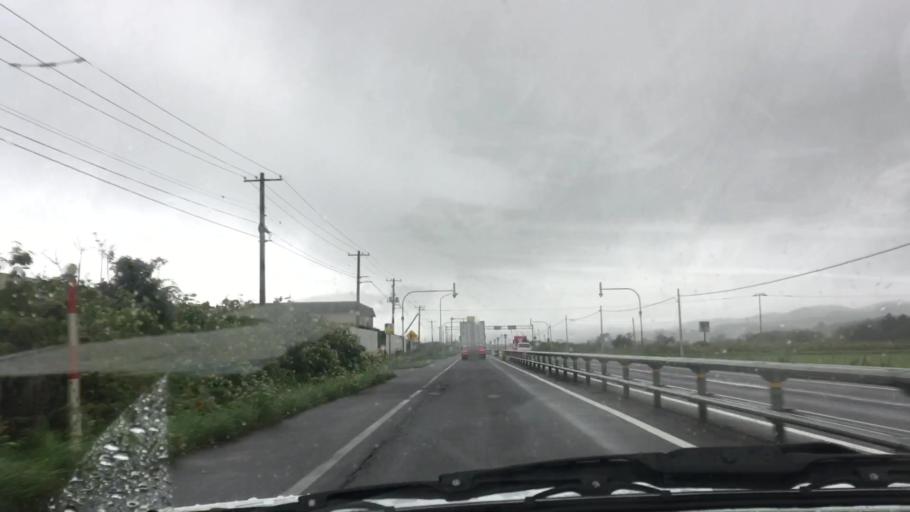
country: JP
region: Hokkaido
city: Niseko Town
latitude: 42.4149
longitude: 140.3094
